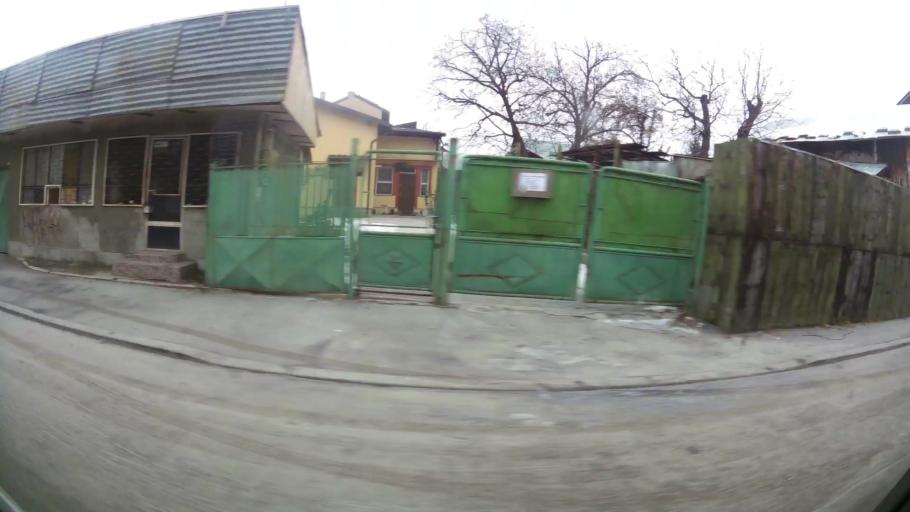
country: RO
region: Prahova
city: Ploiesti
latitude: 44.9425
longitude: 26.0380
